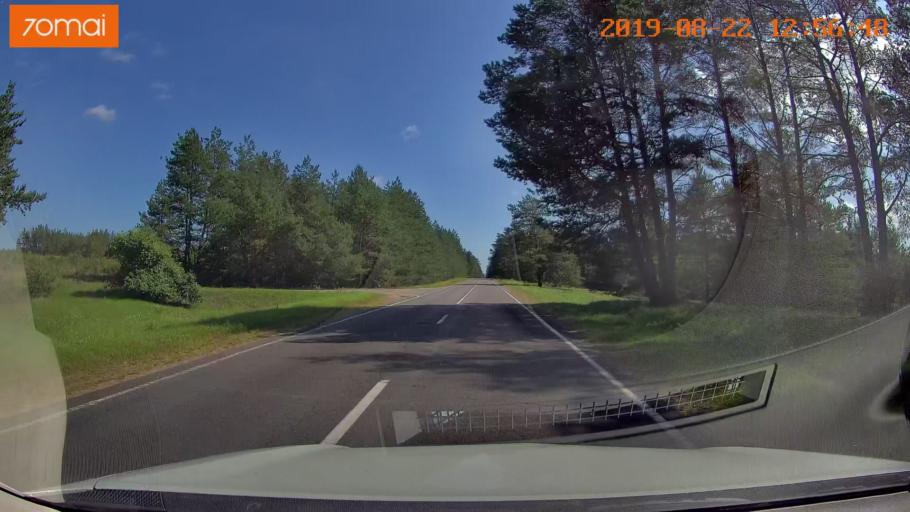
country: BY
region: Minsk
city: Prawdzinski
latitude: 53.4316
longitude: 27.7370
